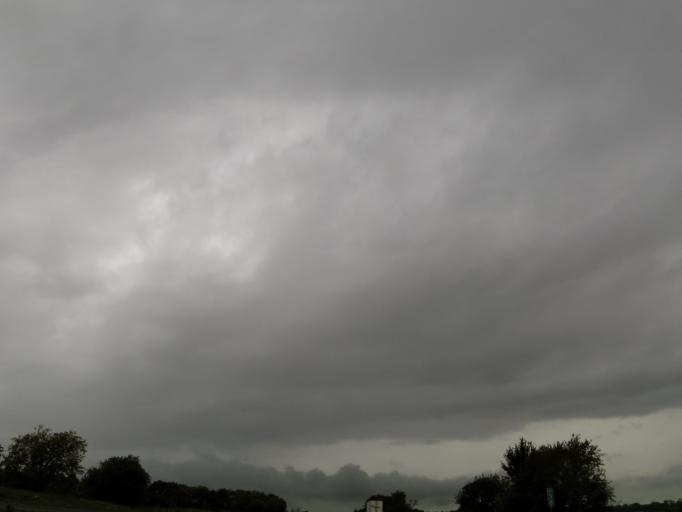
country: US
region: Illinois
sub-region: Clinton County
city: Wamac
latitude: 38.3895
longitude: -89.2238
